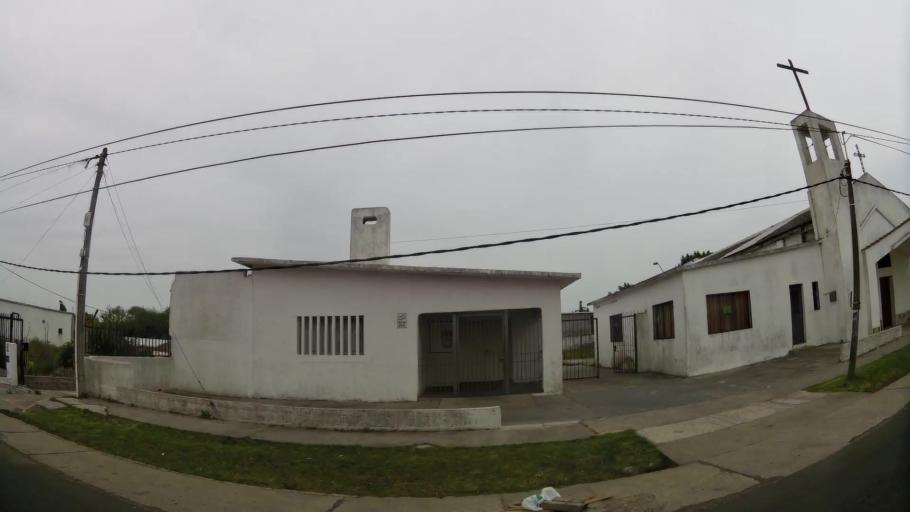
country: UY
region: Canelones
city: Las Piedras
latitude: -34.7325
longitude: -56.2278
